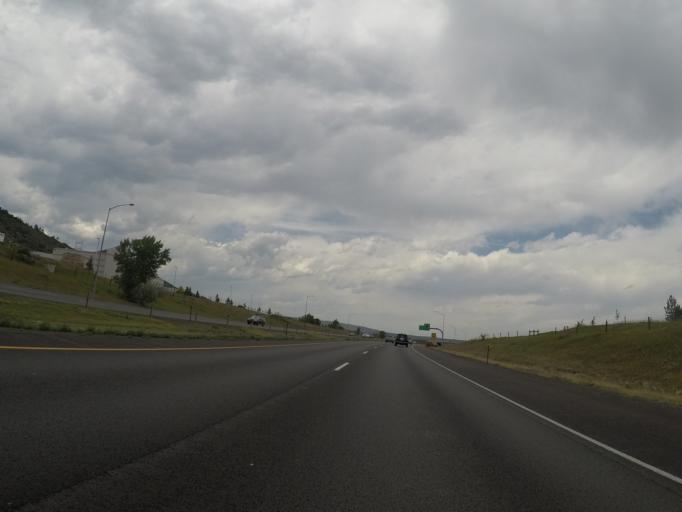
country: US
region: Colorado
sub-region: Jefferson County
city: Ken Caryl
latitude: 39.6048
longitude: -105.1538
